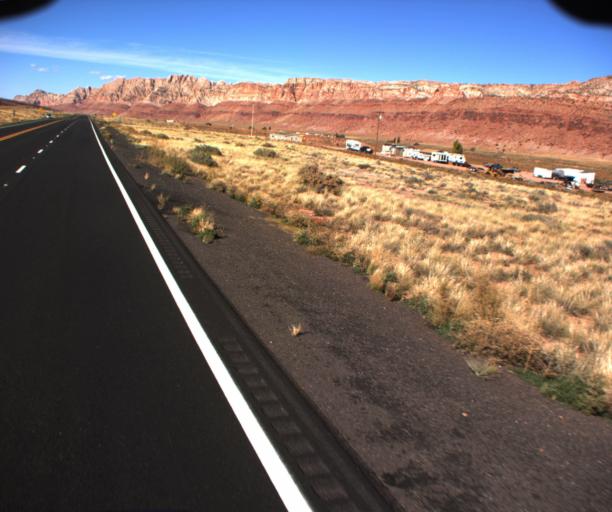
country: US
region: Arizona
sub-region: Coconino County
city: LeChee
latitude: 36.4663
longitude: -111.5683
